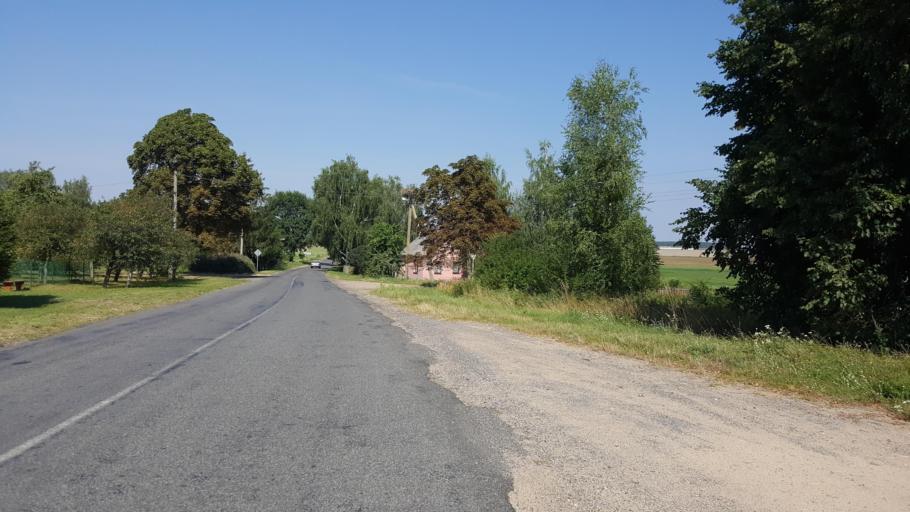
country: BY
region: Brest
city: Kamyanyets
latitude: 52.4661
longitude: 23.7157
